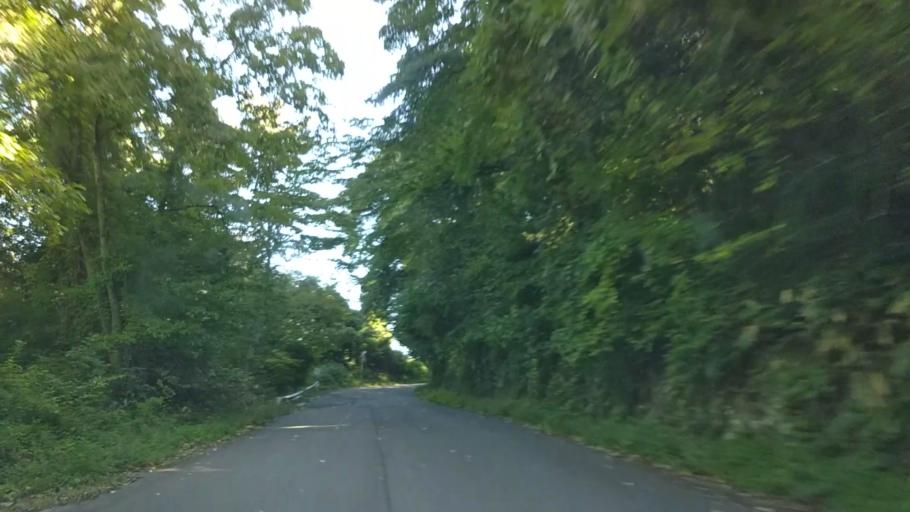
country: JP
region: Nagano
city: Nagano-shi
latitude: 36.5830
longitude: 138.0982
